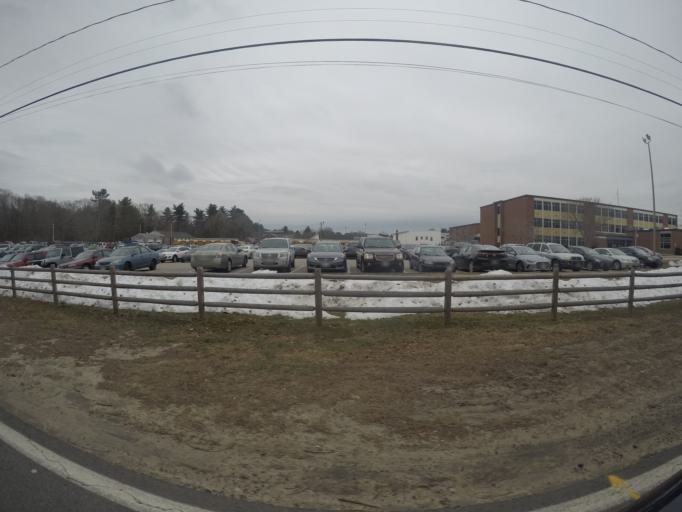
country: US
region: Massachusetts
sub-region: Bristol County
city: Easton
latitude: 42.0102
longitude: -71.0794
